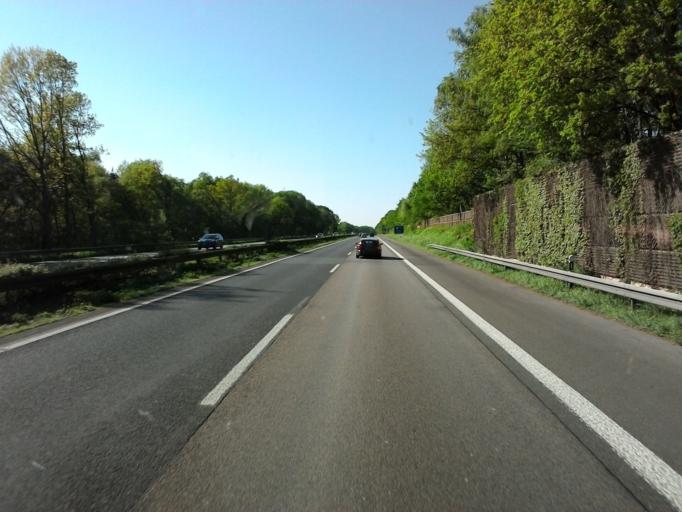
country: DE
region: North Rhine-Westphalia
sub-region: Regierungsbezirk Dusseldorf
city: Hunxe
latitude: 51.6222
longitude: 6.7608
